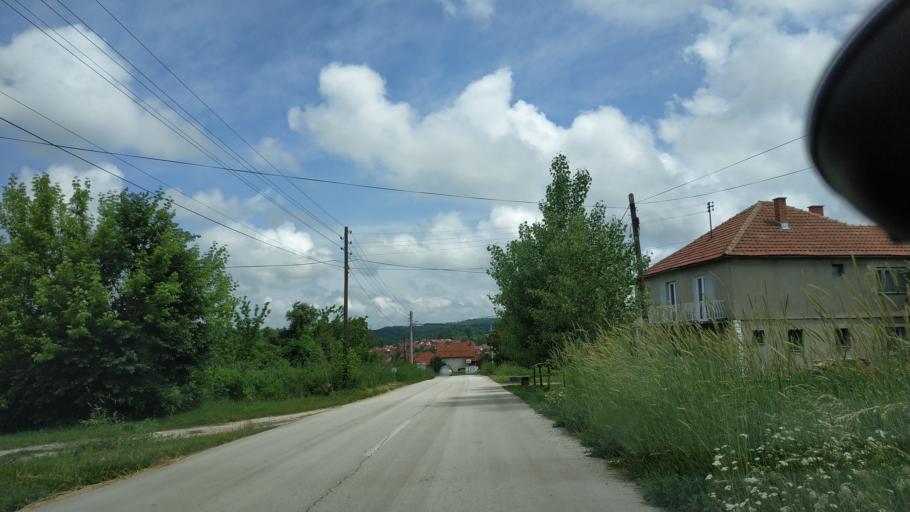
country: RS
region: Central Serbia
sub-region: Zajecarski Okrug
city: Boljevac
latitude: 43.8257
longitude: 21.9574
